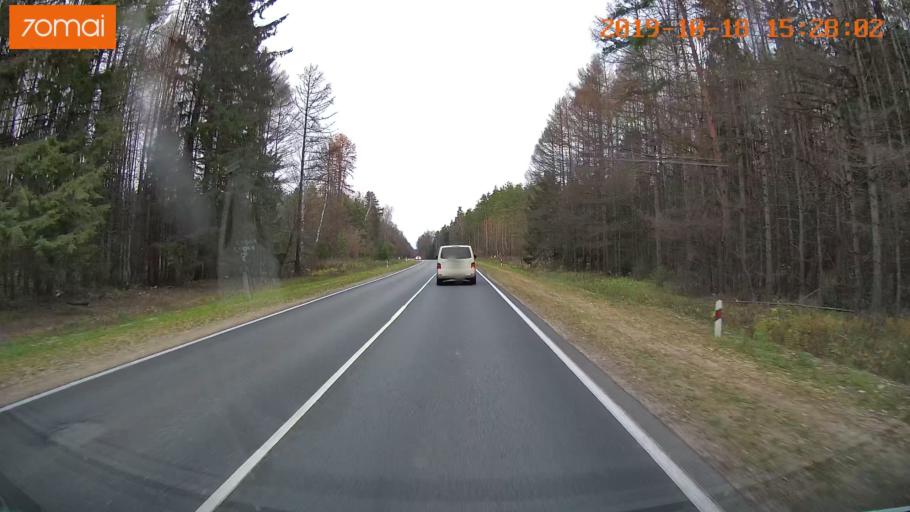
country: RU
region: Vladimir
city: Anopino
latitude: 55.7613
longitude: 40.6732
